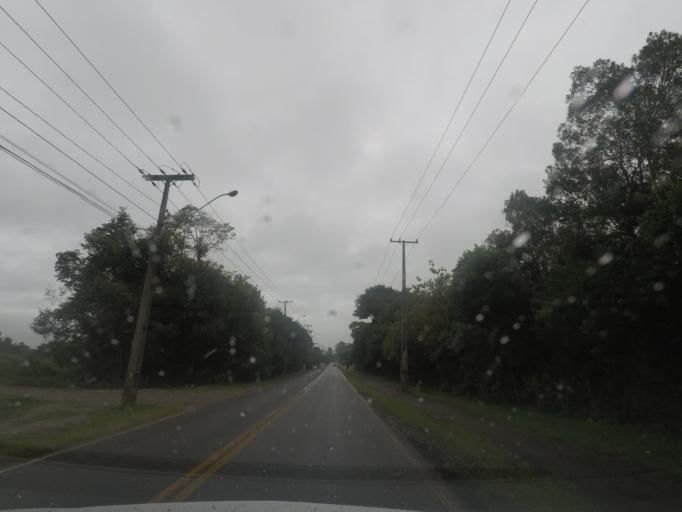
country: BR
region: Parana
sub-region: Quatro Barras
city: Quatro Barras
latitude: -25.3713
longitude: -49.0854
